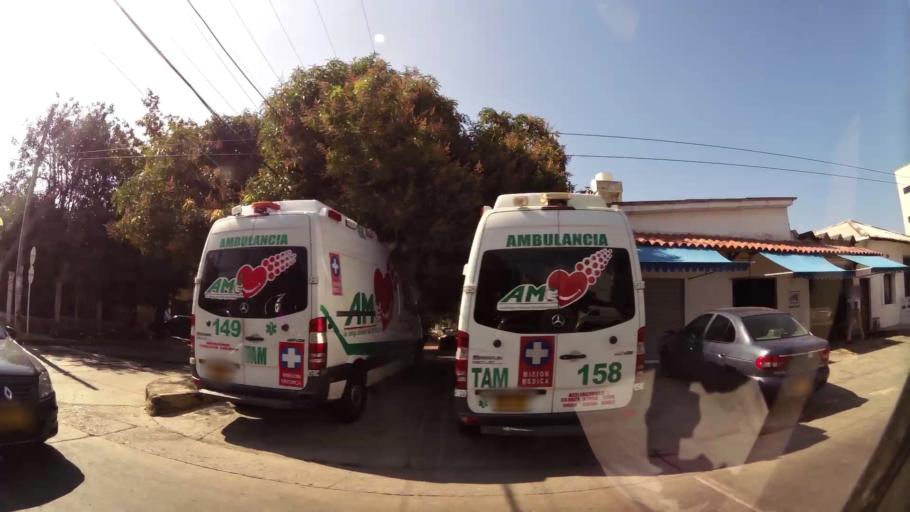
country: CO
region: Atlantico
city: Barranquilla
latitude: 10.9926
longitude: -74.7990
